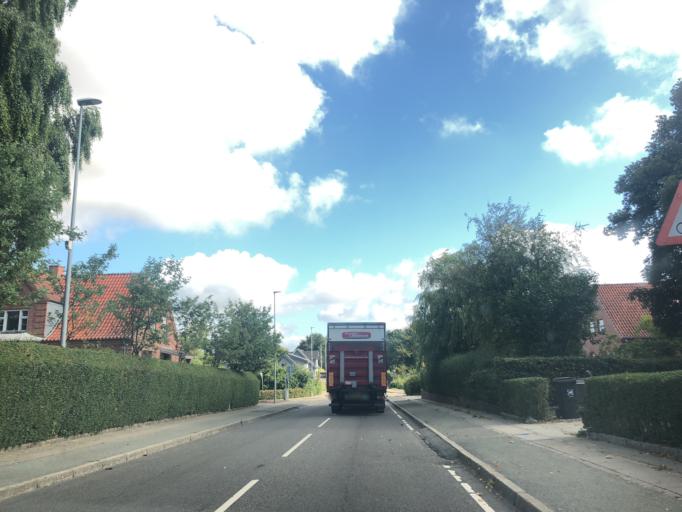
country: DK
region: Central Jutland
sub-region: Skive Kommune
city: Skive
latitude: 56.6508
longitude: 8.9328
